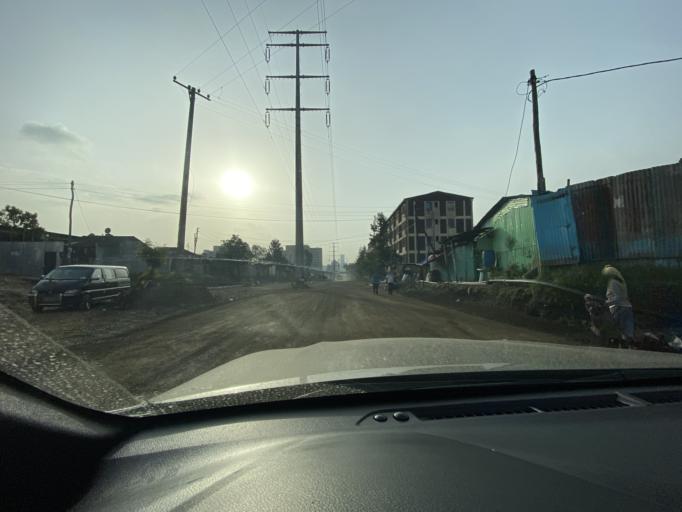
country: ET
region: Adis Abeba
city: Addis Ababa
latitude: 9.0165
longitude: 38.7323
